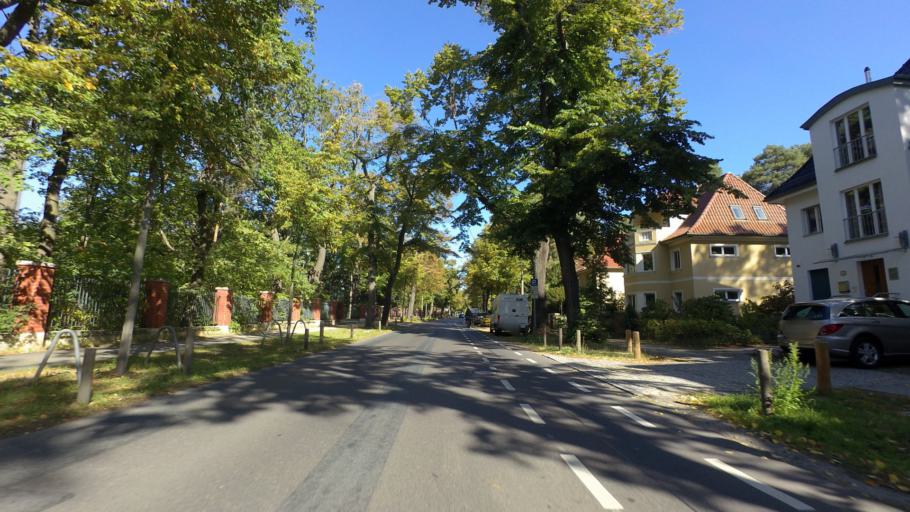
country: DE
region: Berlin
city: Wannsee
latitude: 52.3887
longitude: 13.1226
